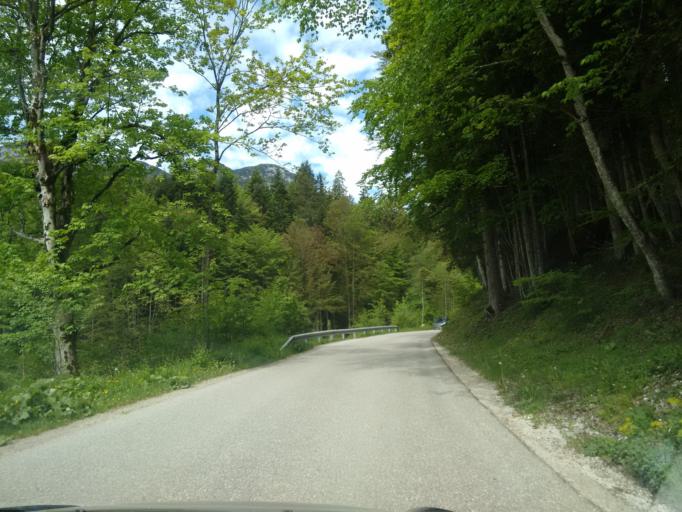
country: AT
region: Styria
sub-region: Politischer Bezirk Liezen
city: Altaussee
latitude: 47.6533
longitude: 13.7491
